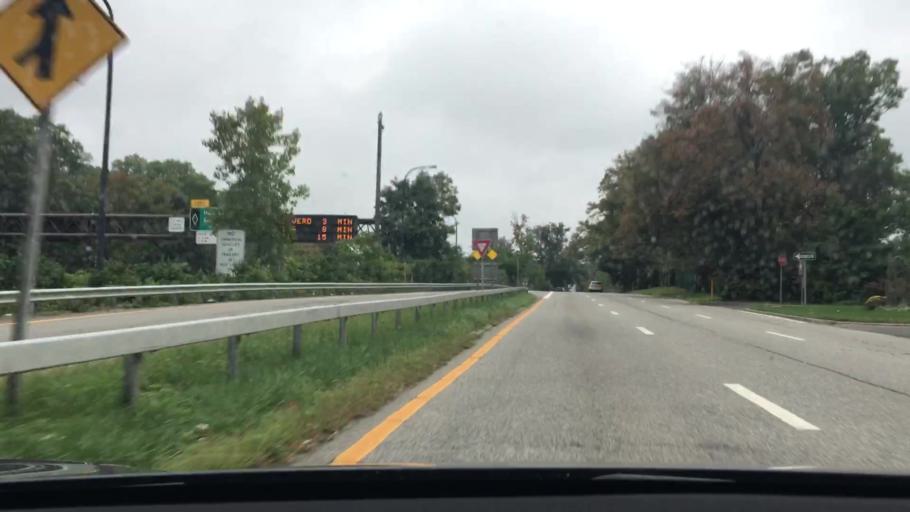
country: US
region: New York
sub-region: Nassau County
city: Manhasset Hills
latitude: 40.7704
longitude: -73.6880
